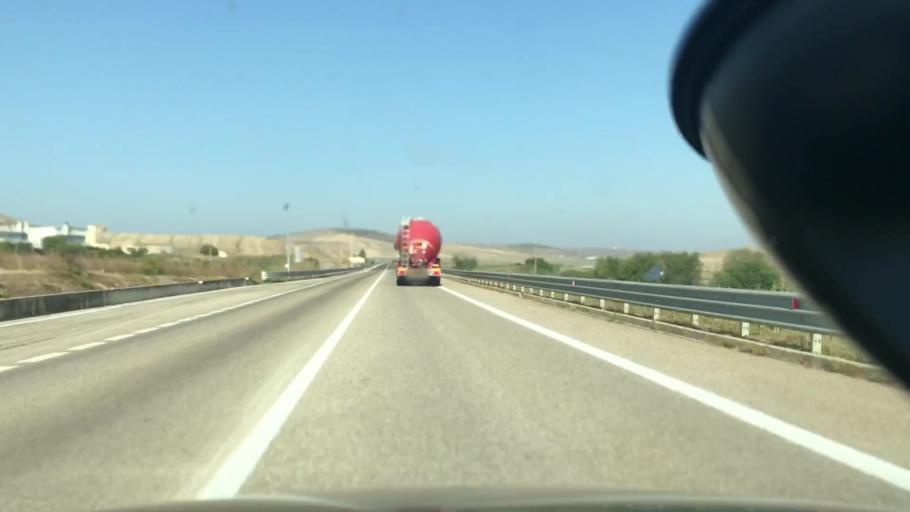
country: IT
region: Basilicate
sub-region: Provincia di Matera
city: Irsina
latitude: 40.7844
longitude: 16.3010
